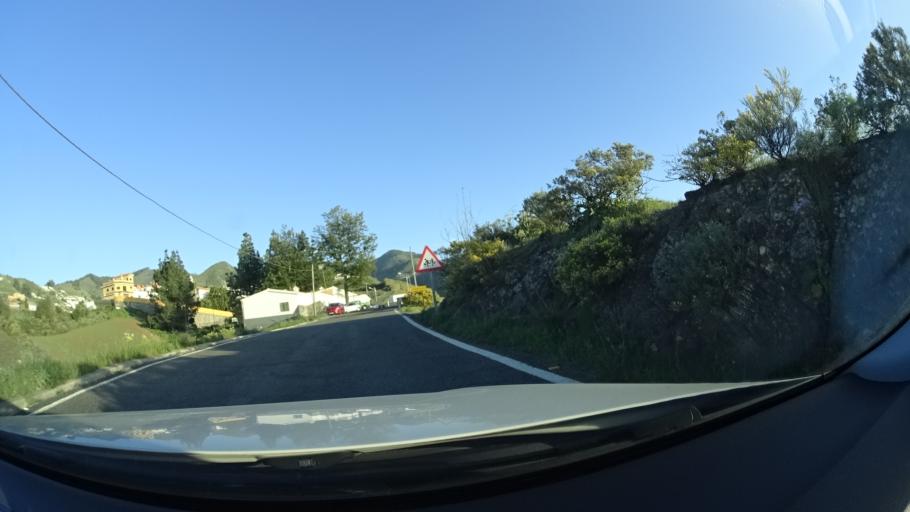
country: ES
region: Canary Islands
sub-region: Provincia de Las Palmas
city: Artenara
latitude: 28.0389
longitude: -15.6469
